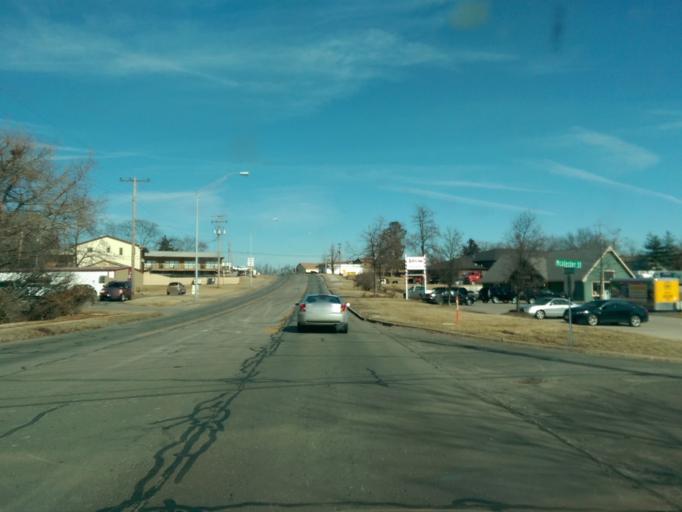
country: US
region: Missouri
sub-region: Boone County
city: Columbia
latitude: 38.9596
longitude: -92.3113
